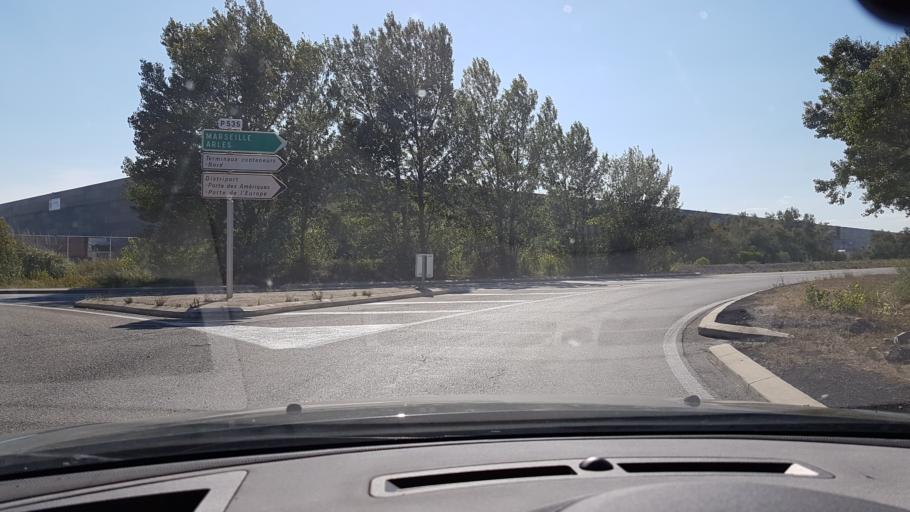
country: FR
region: Provence-Alpes-Cote d'Azur
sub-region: Departement des Bouches-du-Rhone
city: Port-Saint-Louis-du-Rhone
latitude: 43.4069
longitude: 4.8329
